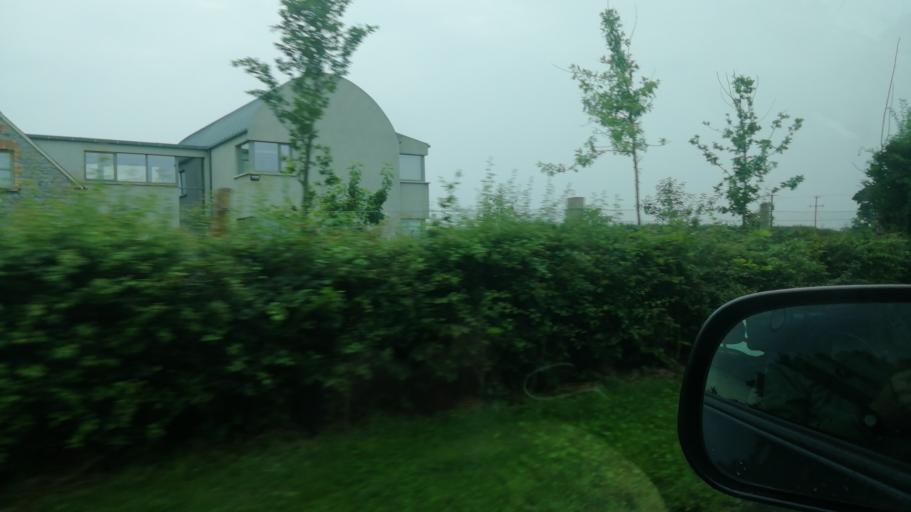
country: IE
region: Leinster
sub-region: Kilkenny
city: Thomastown
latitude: 52.5987
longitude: -7.1544
